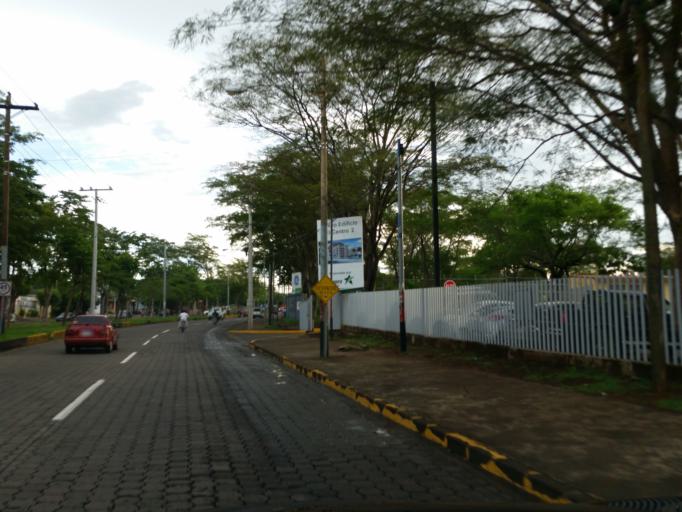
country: NI
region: Managua
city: Managua
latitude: 12.1286
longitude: -86.2812
